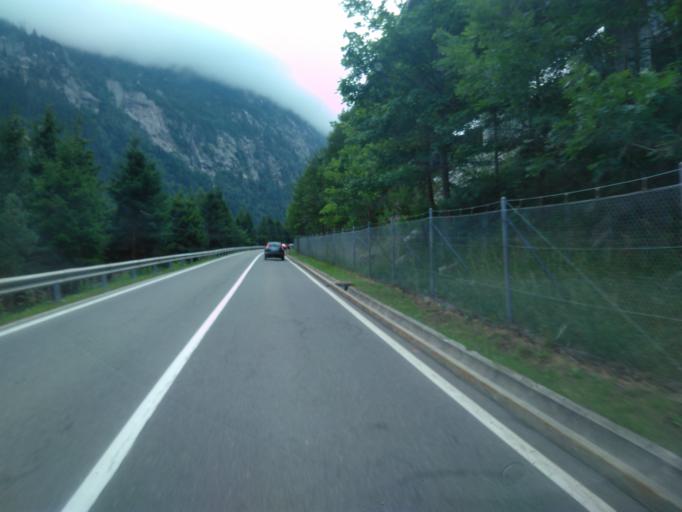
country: CH
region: Uri
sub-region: Uri
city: Andermatt
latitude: 46.6759
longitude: 8.5933
